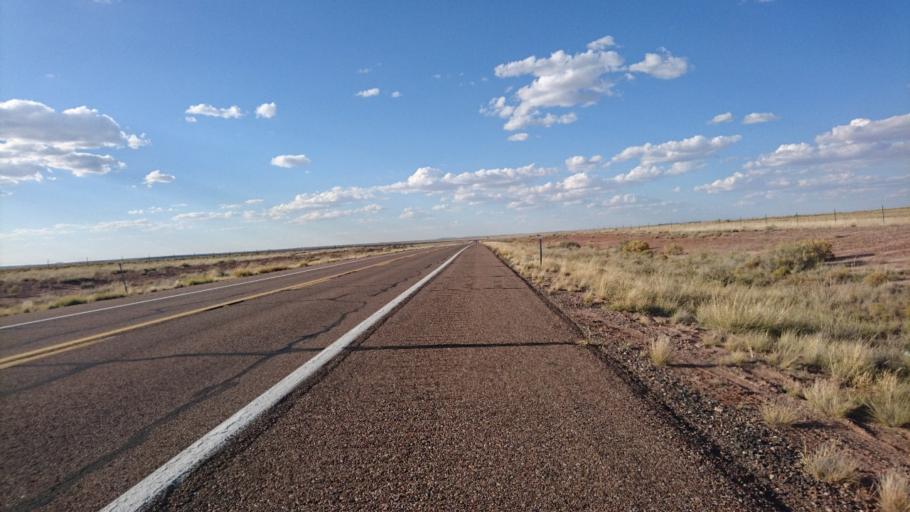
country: US
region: Arizona
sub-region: Navajo County
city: Holbrook
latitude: 34.8119
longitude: -109.9188
